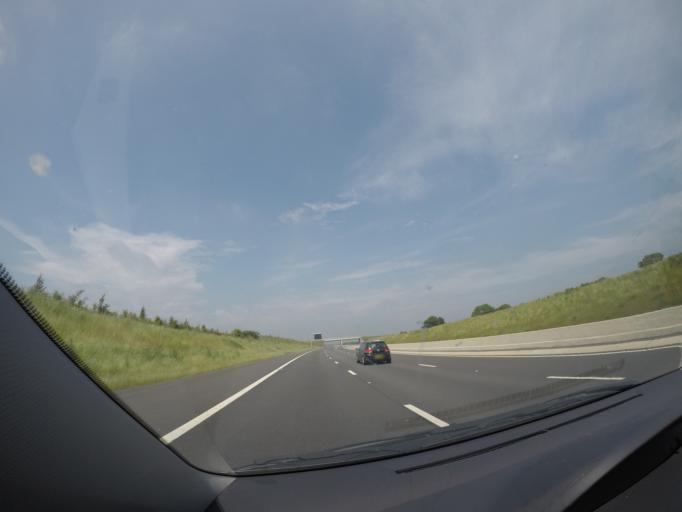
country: GB
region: England
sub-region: North Yorkshire
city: Catterick
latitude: 54.3668
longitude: -1.6337
